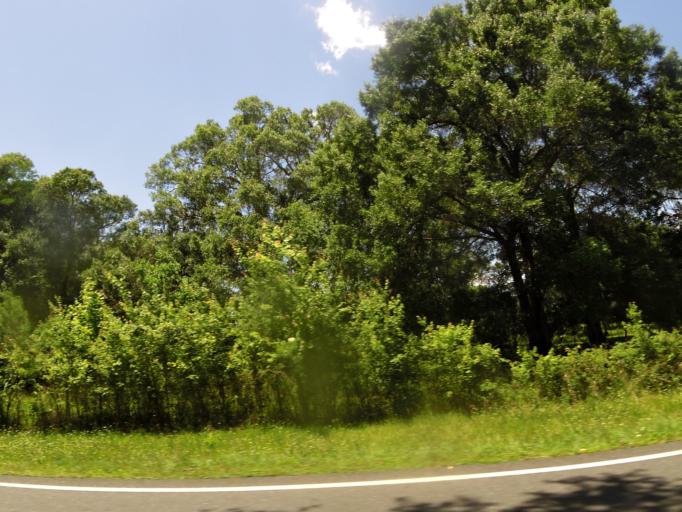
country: US
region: Florida
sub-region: Union County
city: Lake Butler
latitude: 30.0567
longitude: -82.2367
